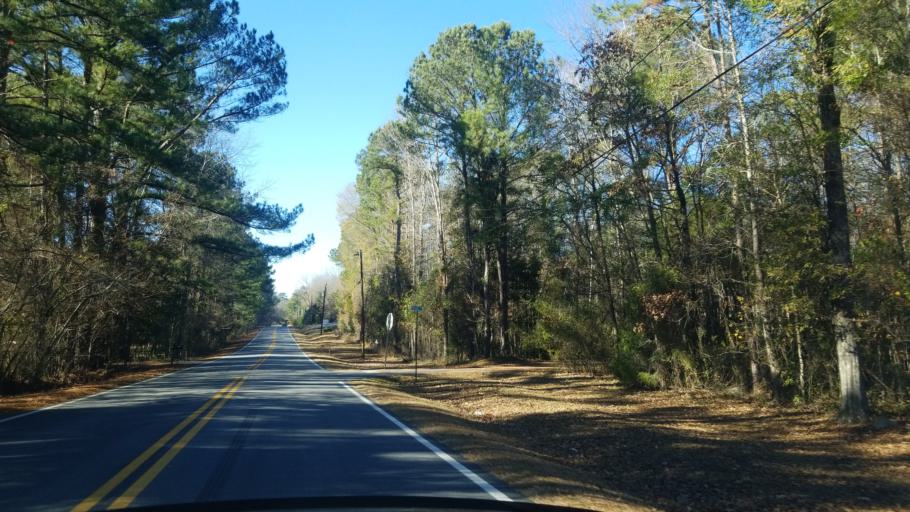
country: US
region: Georgia
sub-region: Harris County
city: Hamilton
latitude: 32.6658
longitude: -84.8721
